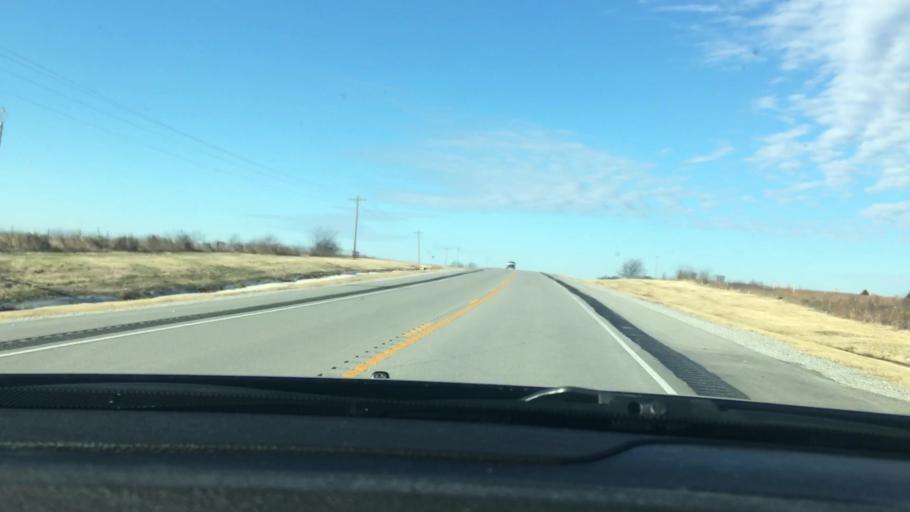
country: US
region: Oklahoma
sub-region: Love County
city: Marietta
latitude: 33.9405
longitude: -97.2267
